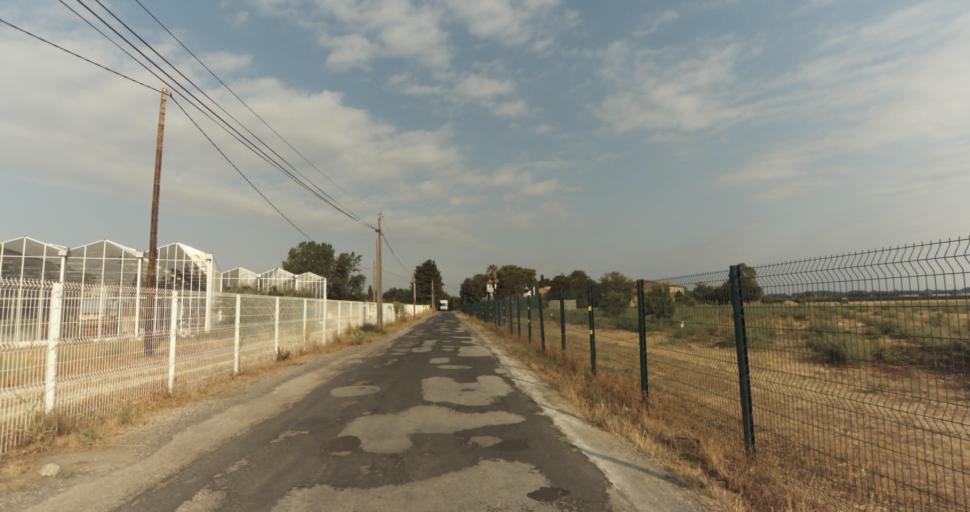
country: FR
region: Languedoc-Roussillon
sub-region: Departement des Pyrenees-Orientales
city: Alenya
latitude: 42.6222
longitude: 2.9748
